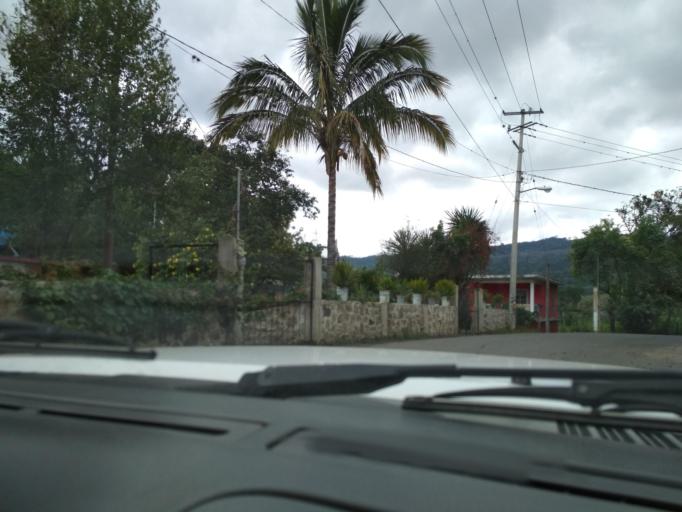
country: MX
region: Veracruz
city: El Castillo
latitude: 19.5839
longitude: -96.8366
